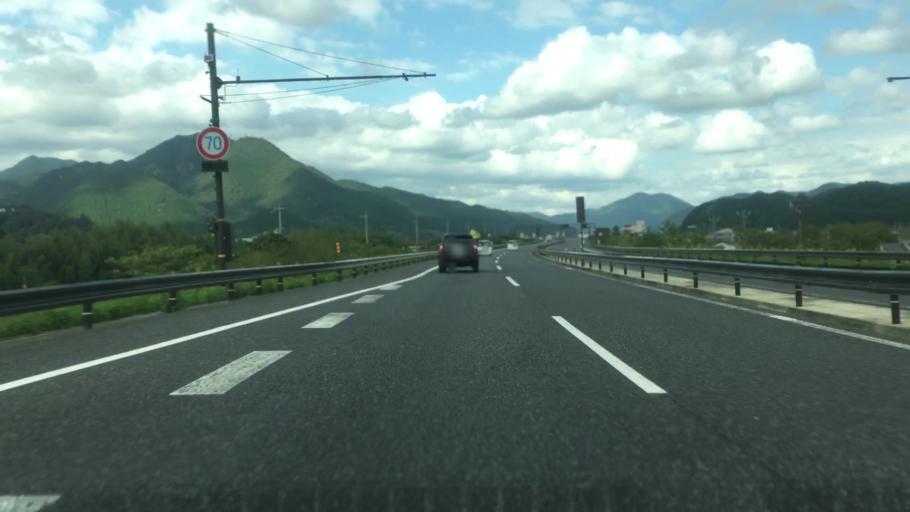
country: JP
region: Kyoto
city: Fukuchiyama
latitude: 35.1663
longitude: 135.0439
